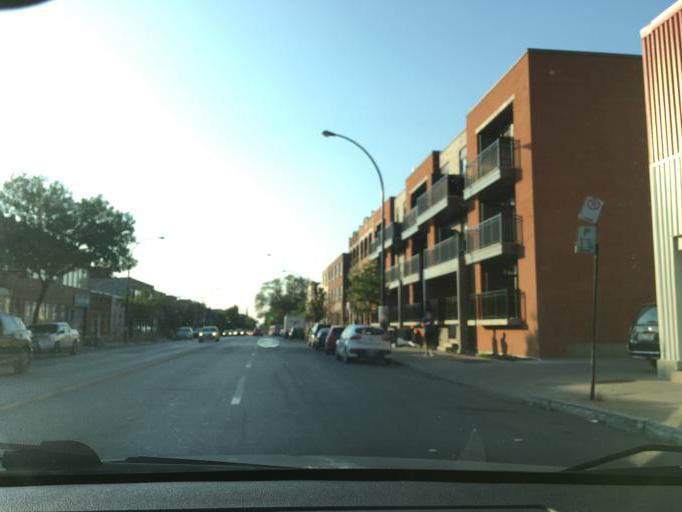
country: CA
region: Quebec
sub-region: Montreal
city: Montreal
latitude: 45.5437
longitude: -73.5979
